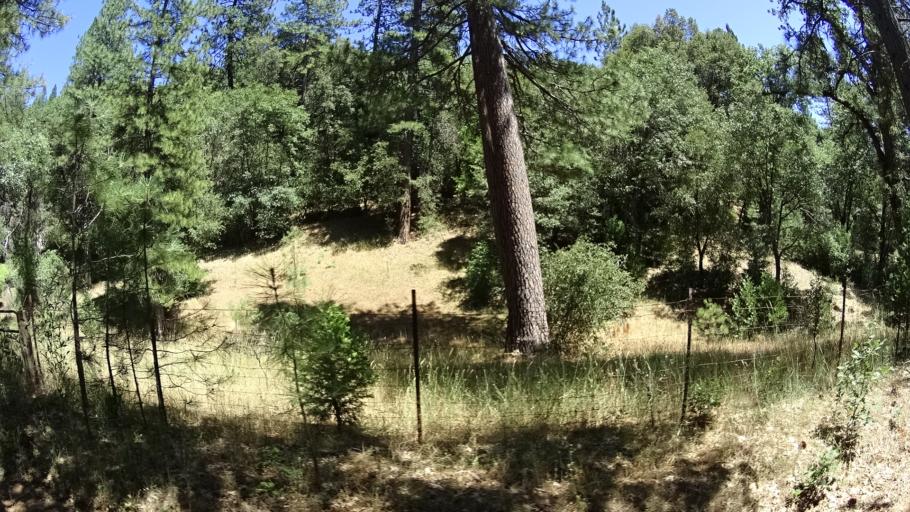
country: US
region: California
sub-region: Calaveras County
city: Mountain Ranch
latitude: 38.3260
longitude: -120.5081
